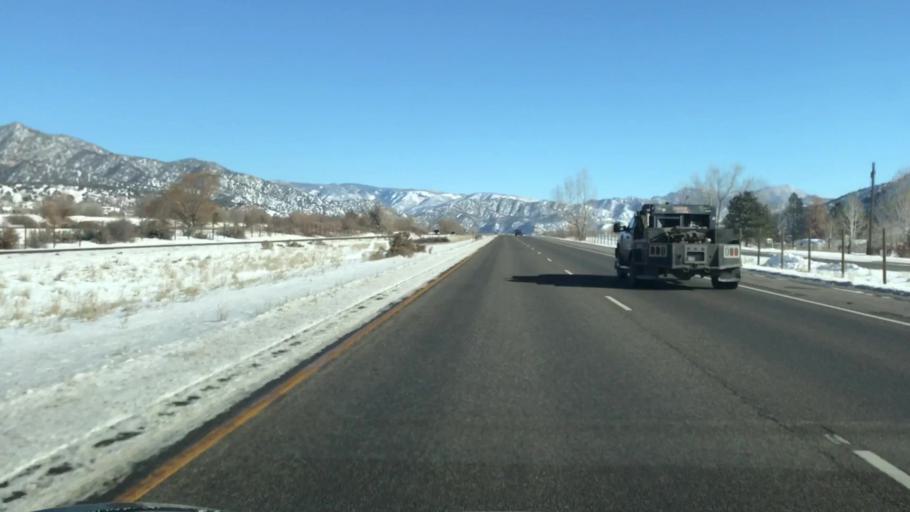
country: US
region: Colorado
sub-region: Garfield County
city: Silt
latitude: 39.5496
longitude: -107.6029
